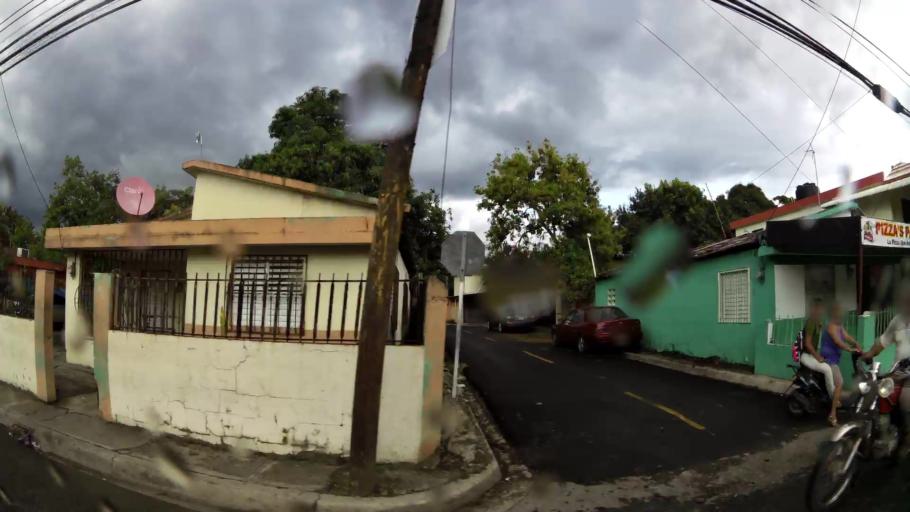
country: DO
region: Monsenor Nouel
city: Bonao
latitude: 18.9306
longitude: -70.4017
